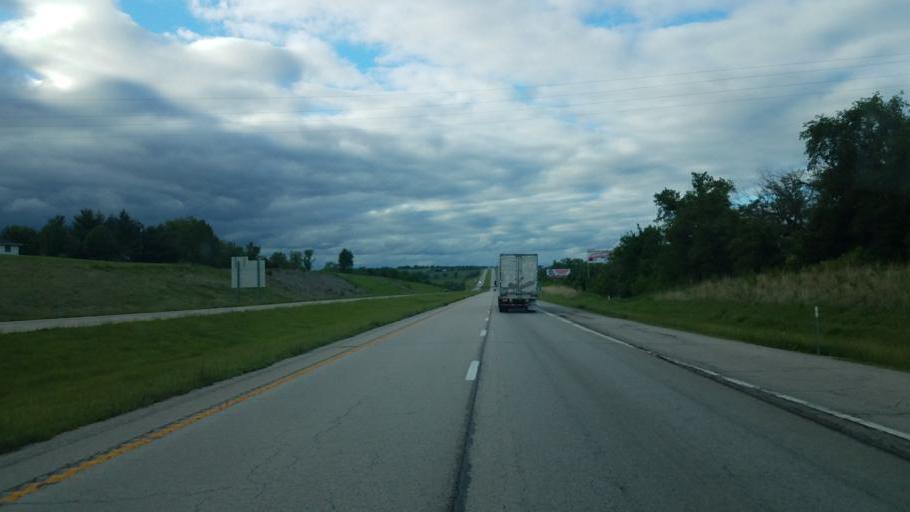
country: US
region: Missouri
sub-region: Harrison County
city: Bethany
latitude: 40.2840
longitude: -94.0122
